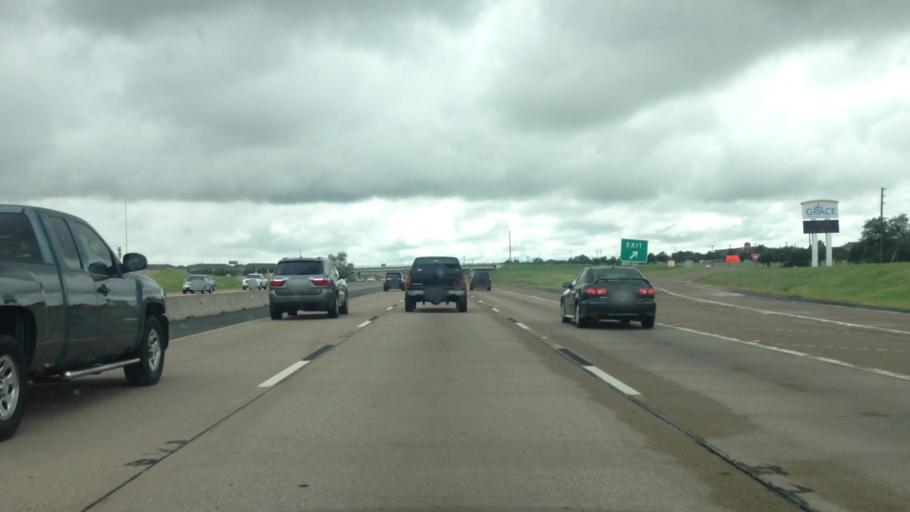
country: US
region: Texas
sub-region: Tarrant County
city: Lake Worth
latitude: 32.7862
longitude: -97.4635
